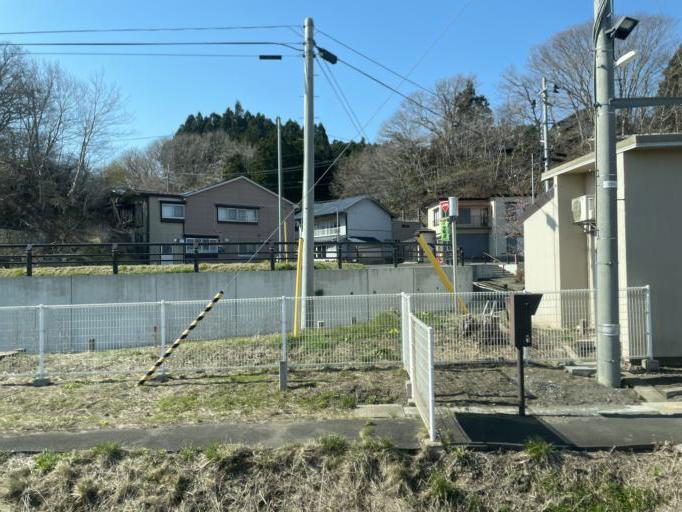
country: JP
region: Aomori
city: Hachinohe
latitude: 40.3452
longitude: 141.7670
